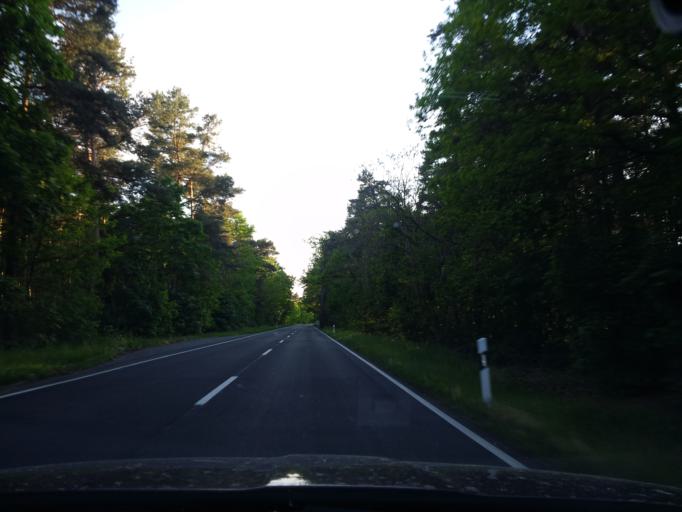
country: DE
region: Brandenburg
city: Luckenwalde
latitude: 52.0523
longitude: 13.1389
